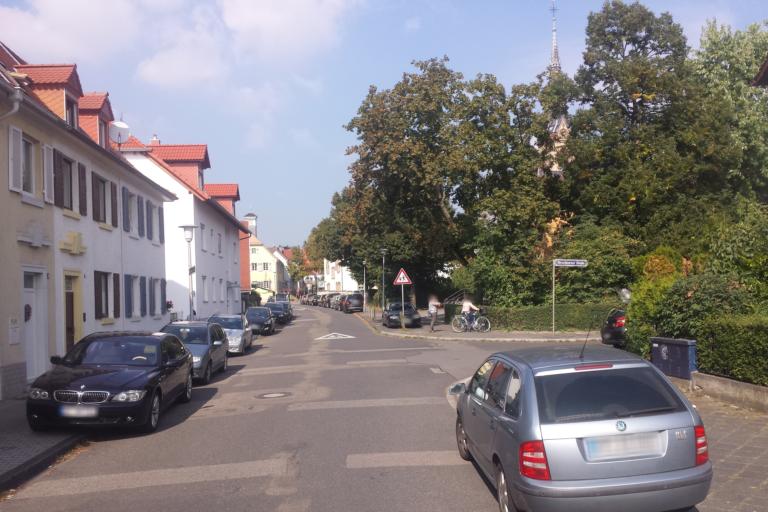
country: DE
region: Baden-Wuerttemberg
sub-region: Karlsruhe Region
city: Ilvesheim
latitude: 49.4853
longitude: 8.5335
